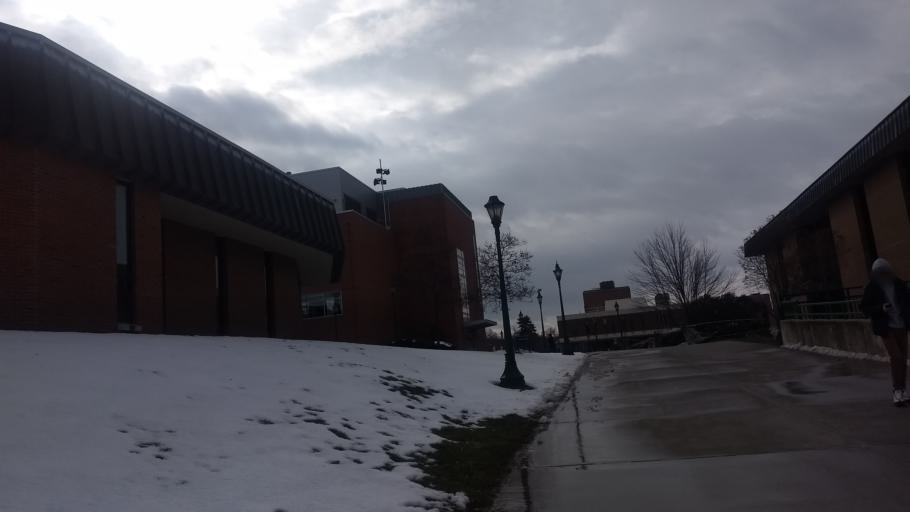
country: US
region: New York
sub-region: Livingston County
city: Geneseo
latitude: 42.7978
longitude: -77.8193
